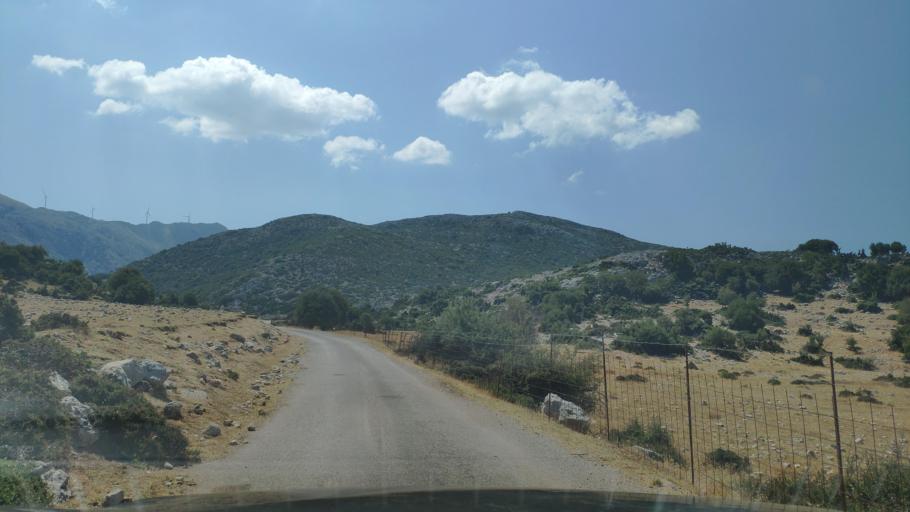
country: GR
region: West Greece
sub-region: Nomos Aitolias kai Akarnanias
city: Monastirakion
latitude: 38.8005
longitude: 20.9483
